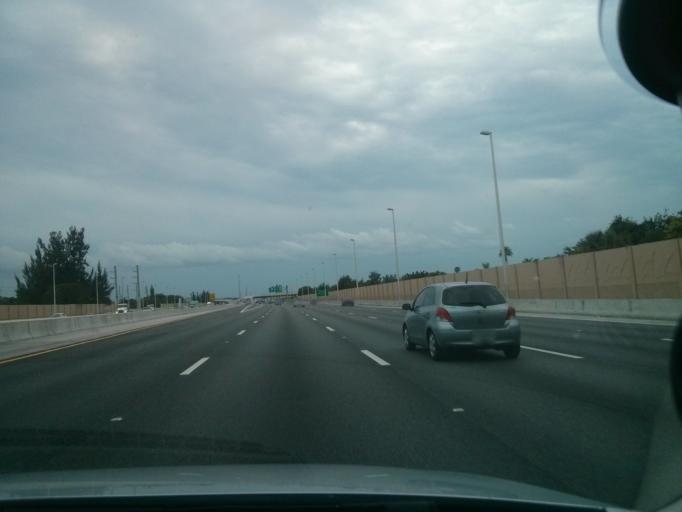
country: US
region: Florida
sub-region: Broward County
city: Broadview Park
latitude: 26.1025
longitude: -80.2182
